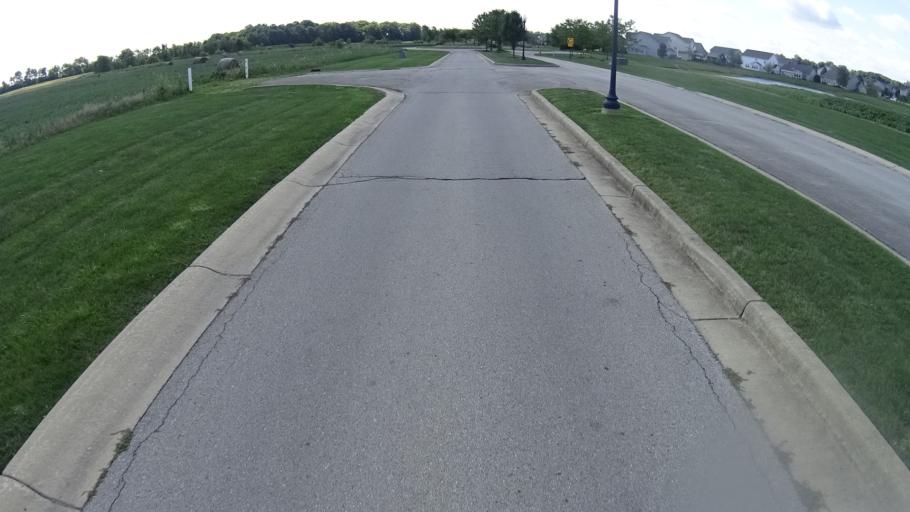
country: US
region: Indiana
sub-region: Madison County
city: Pendleton
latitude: 39.9848
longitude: -85.7450
